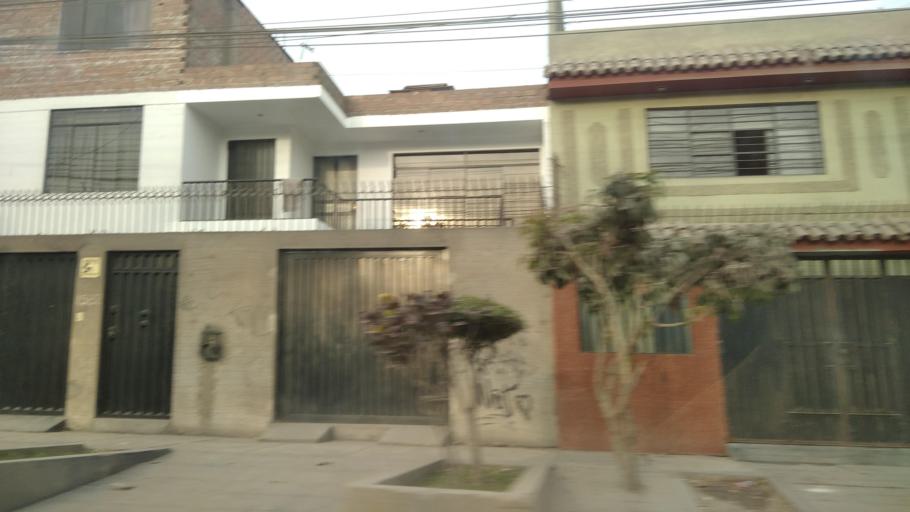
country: PE
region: Lima
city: Lima
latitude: -12.0064
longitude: -77.0010
